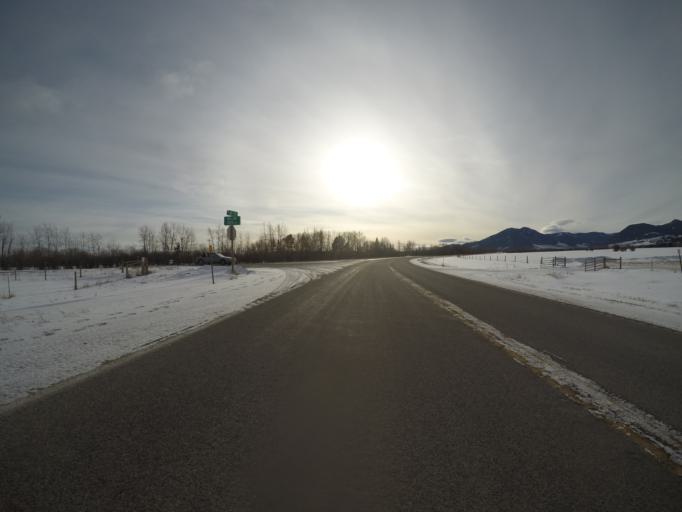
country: US
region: Montana
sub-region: Carbon County
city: Red Lodge
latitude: 45.2096
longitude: -109.2613
